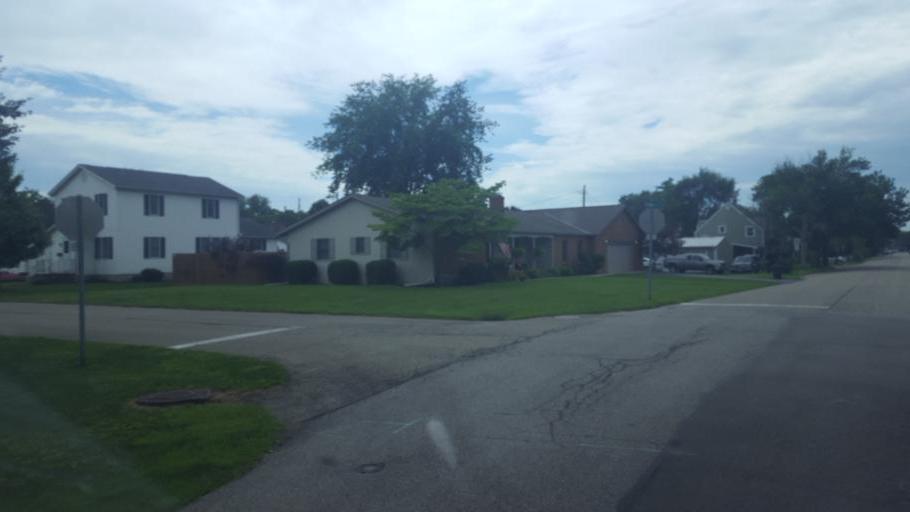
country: US
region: Ohio
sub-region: Pickaway County
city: Ashville
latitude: 39.7152
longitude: -82.9469
